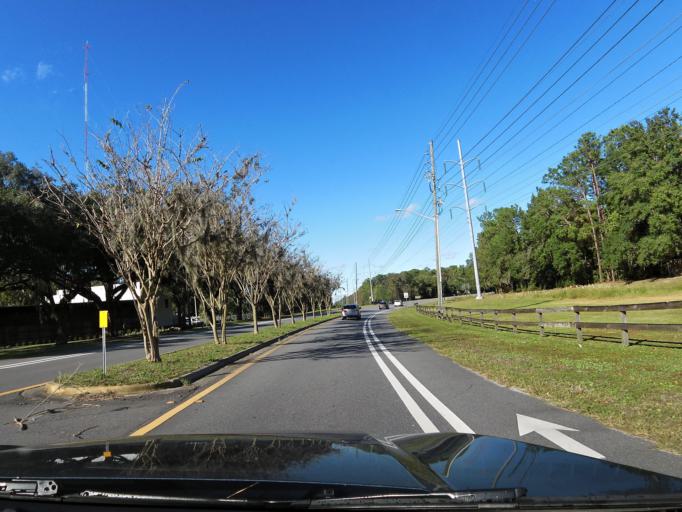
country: US
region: Florida
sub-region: Alachua County
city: Alachua
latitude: 29.7093
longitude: -82.3891
